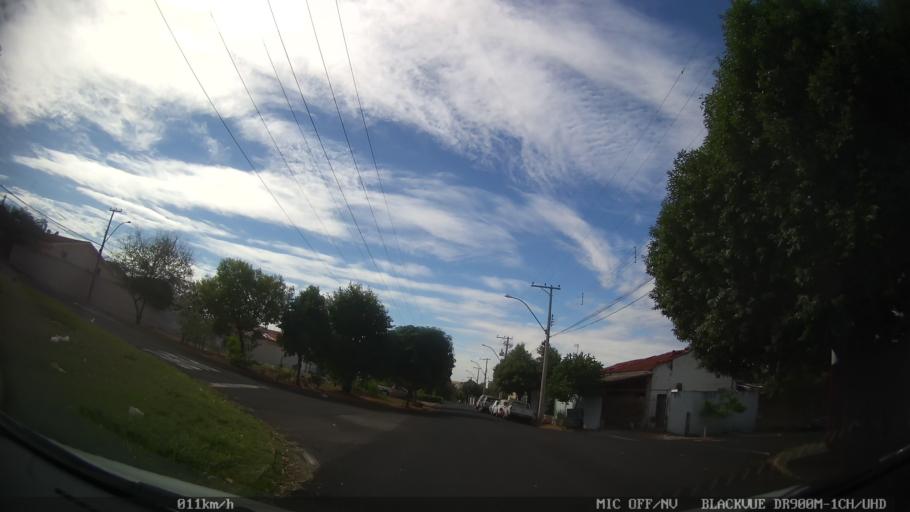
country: BR
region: Sao Paulo
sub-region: Sao Jose Do Rio Preto
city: Sao Jose do Rio Preto
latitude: -20.8344
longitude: -49.3511
